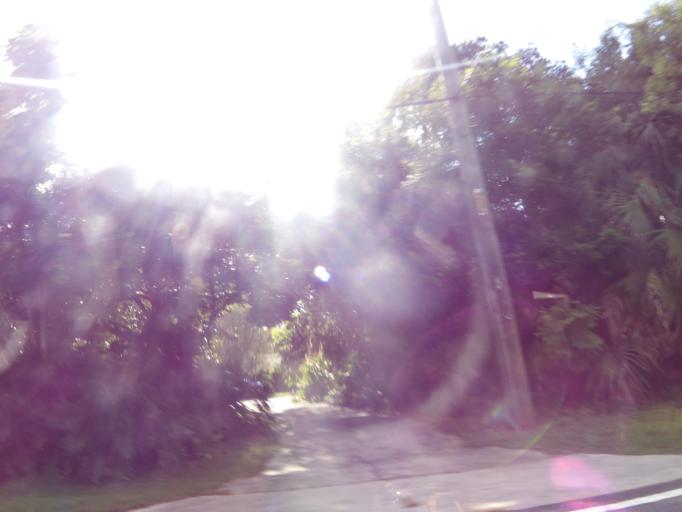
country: US
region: Florida
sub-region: Duval County
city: Jacksonville
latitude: 30.2846
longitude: -81.7388
